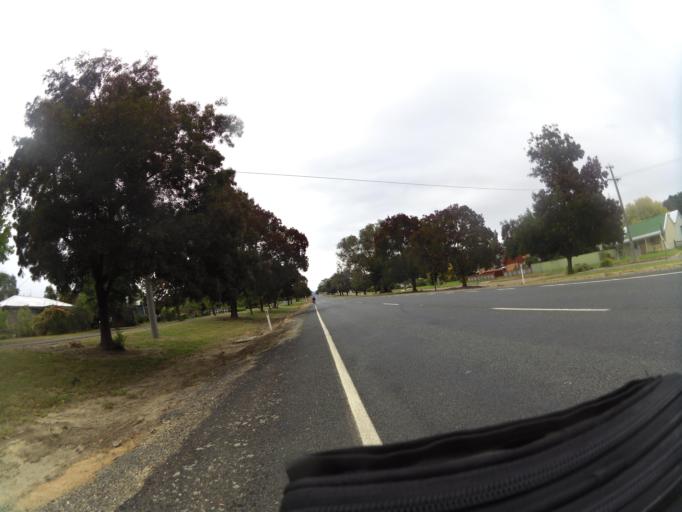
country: AU
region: New South Wales
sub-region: Snowy River
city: Jindabyne
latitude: -36.1882
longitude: 147.9158
